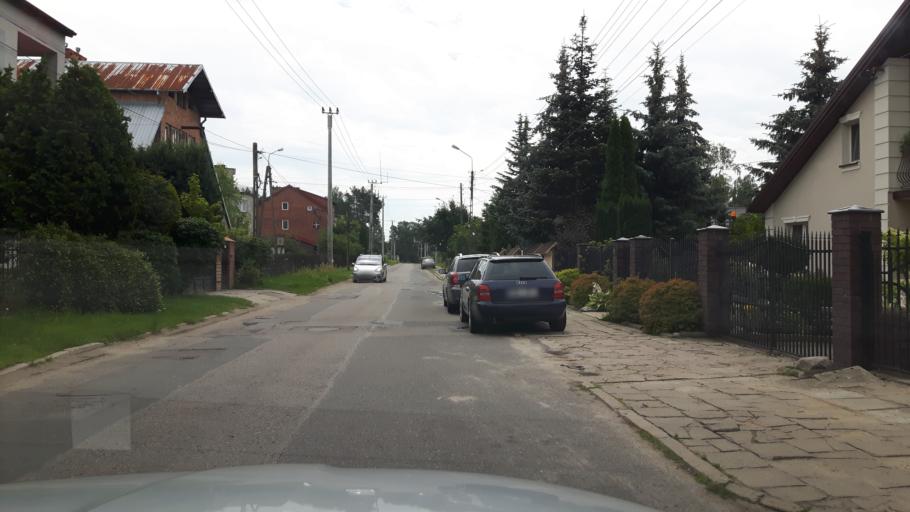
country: PL
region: Masovian Voivodeship
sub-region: Powiat wolominski
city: Wolomin
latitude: 52.3219
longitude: 21.2198
